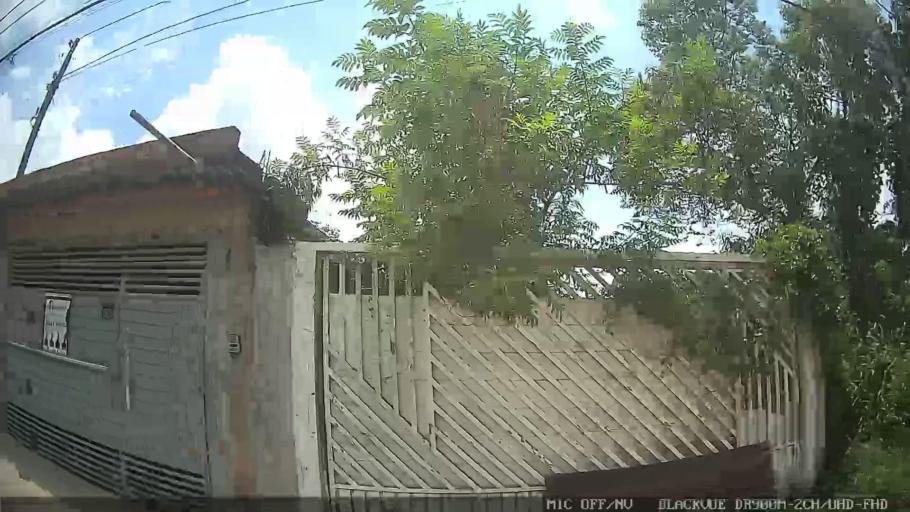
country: BR
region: Sao Paulo
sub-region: Ferraz De Vasconcelos
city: Ferraz de Vasconcelos
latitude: -23.5708
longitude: -46.3661
